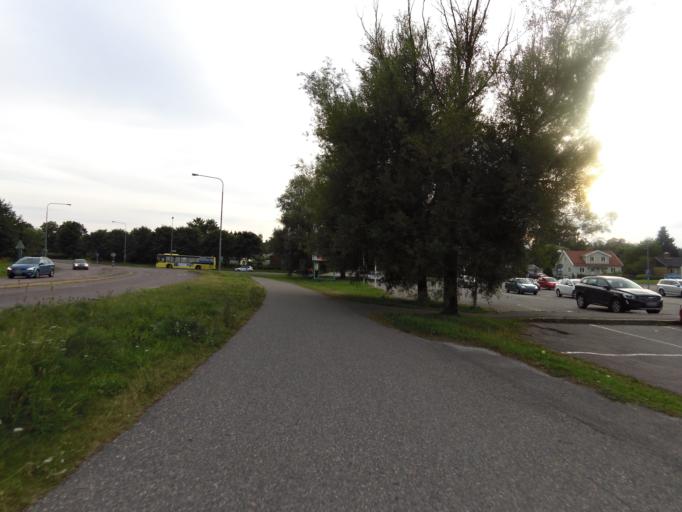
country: SE
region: Gaevleborg
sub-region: Gavle Kommun
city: Gavle
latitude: 60.7010
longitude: 17.1543
